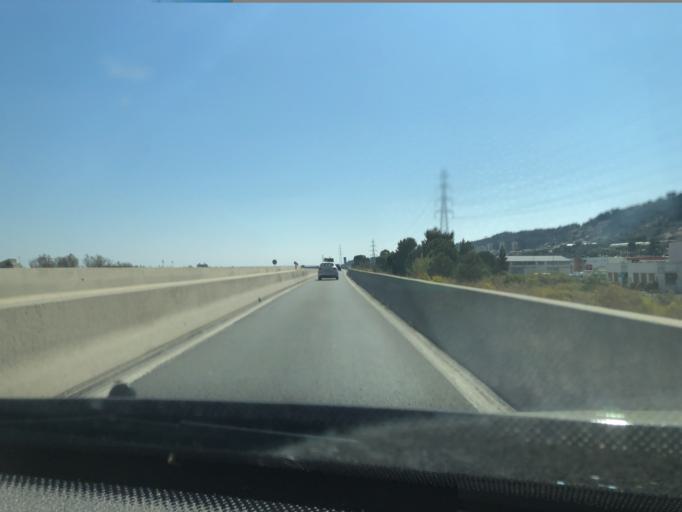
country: FR
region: Provence-Alpes-Cote d'Azur
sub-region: Departement des Alpes-Maritimes
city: Saint-Laurent-du-Var
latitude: 43.7021
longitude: 7.1851
